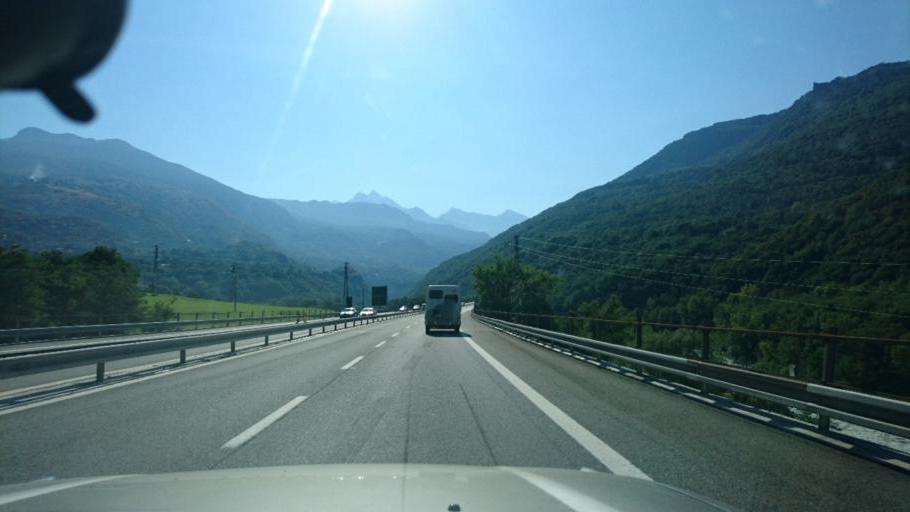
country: IT
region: Aosta Valley
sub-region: Valle d'Aosta
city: Chatillon
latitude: 45.7460
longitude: 7.6323
